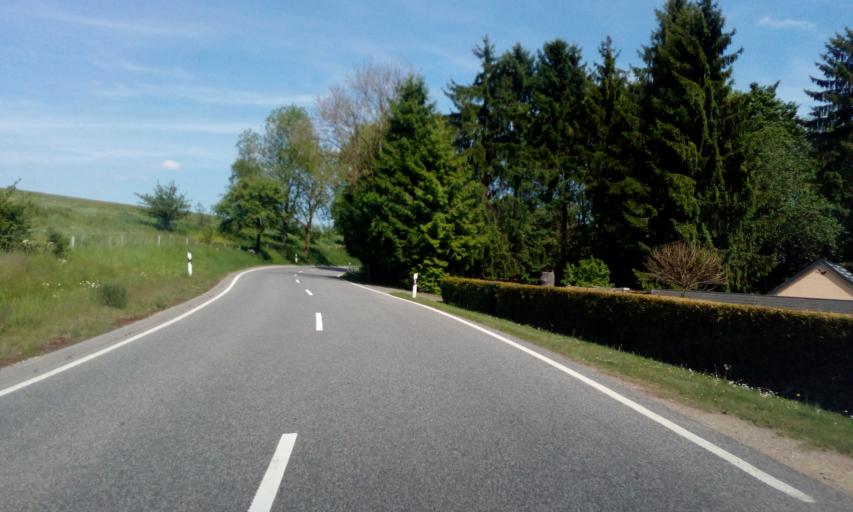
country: DE
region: Rheinland-Pfalz
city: Korperich
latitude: 49.9291
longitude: 6.2438
